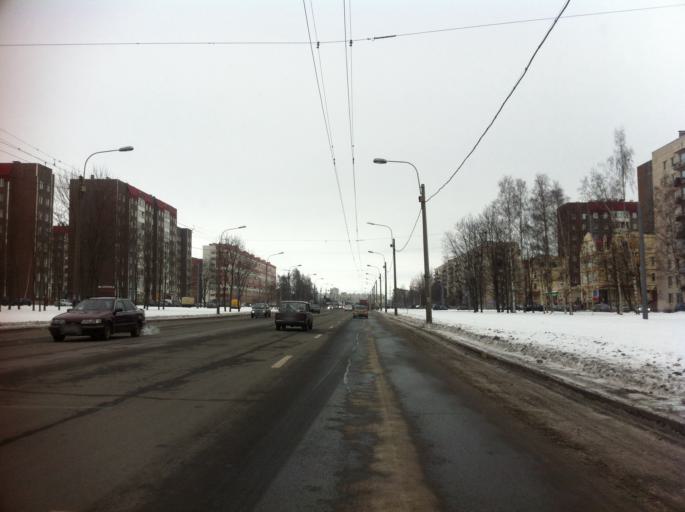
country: RU
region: St.-Petersburg
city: Uritsk
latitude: 59.8368
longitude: 30.1757
